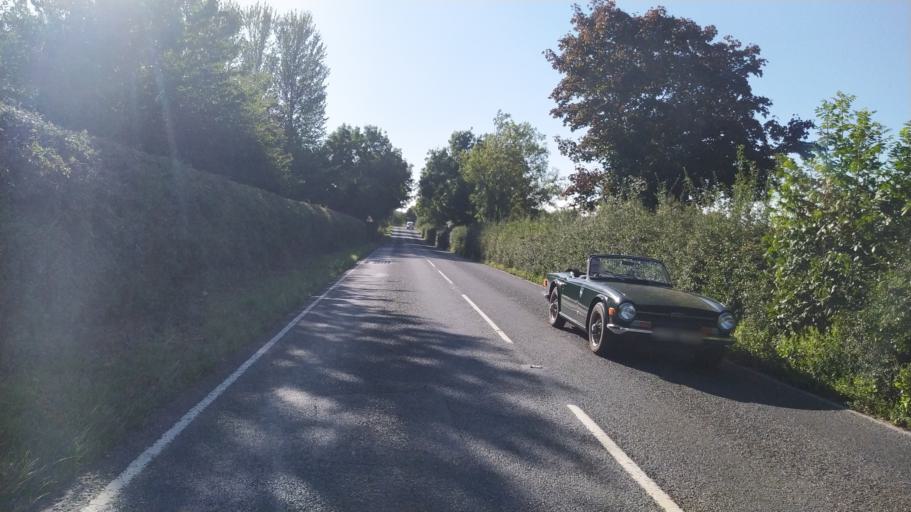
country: GB
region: England
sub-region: Hampshire
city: Alton
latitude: 51.1375
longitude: -0.9346
